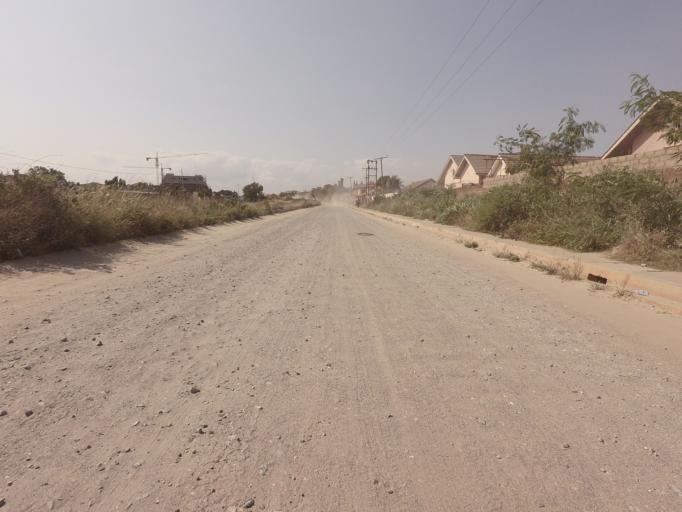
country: GH
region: Greater Accra
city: Teshi Old Town
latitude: 5.6296
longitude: -0.1241
